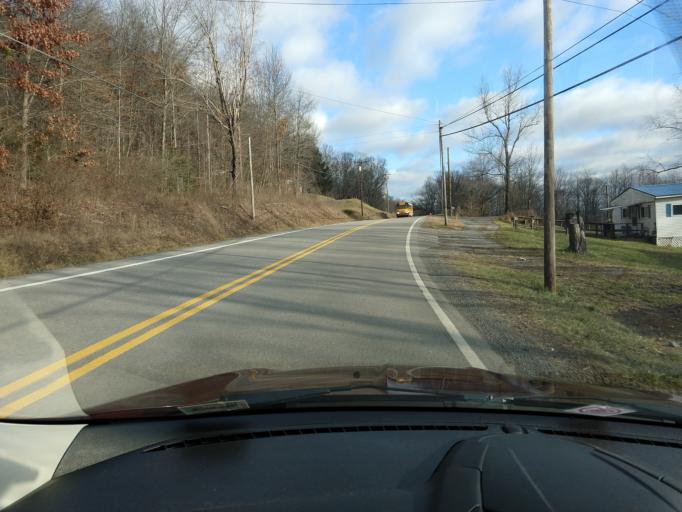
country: US
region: West Virginia
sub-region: Randolph County
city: Elkins
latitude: 38.7446
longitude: -79.9640
